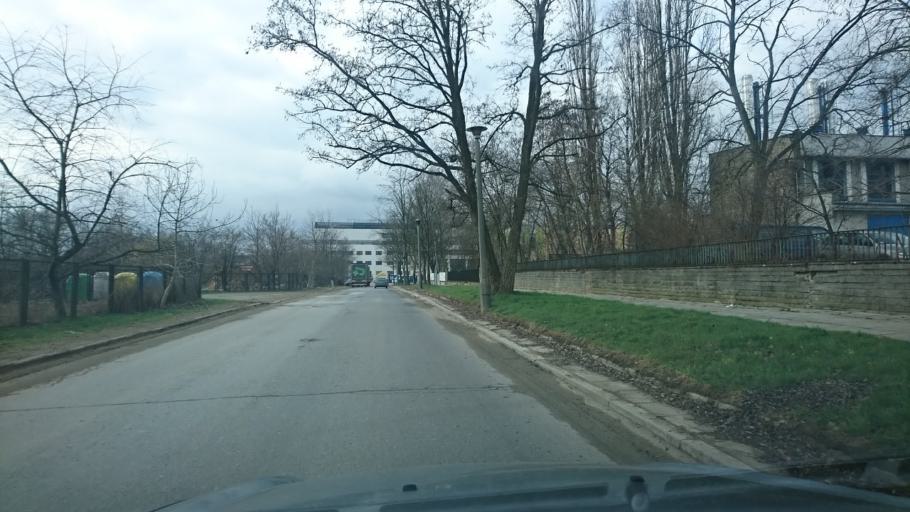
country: PL
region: Lesser Poland Voivodeship
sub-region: Powiat wielicki
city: Czarnochowice
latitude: 50.0107
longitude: 20.0038
